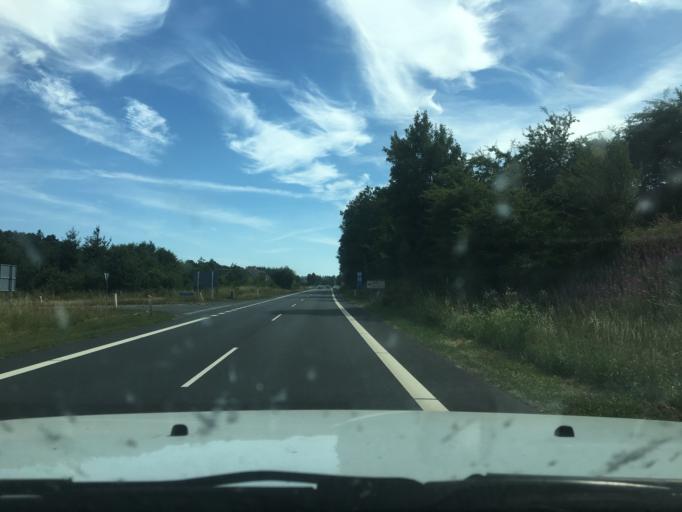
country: DK
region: Central Jutland
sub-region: Viborg Kommune
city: Viborg
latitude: 56.5267
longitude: 9.4046
